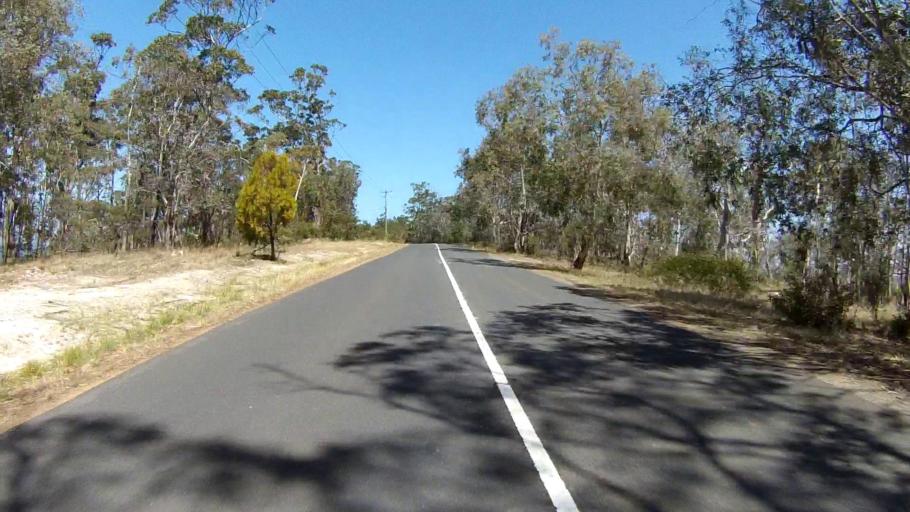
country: AU
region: Tasmania
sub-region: Clarence
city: Sandford
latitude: -43.0119
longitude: 147.4806
